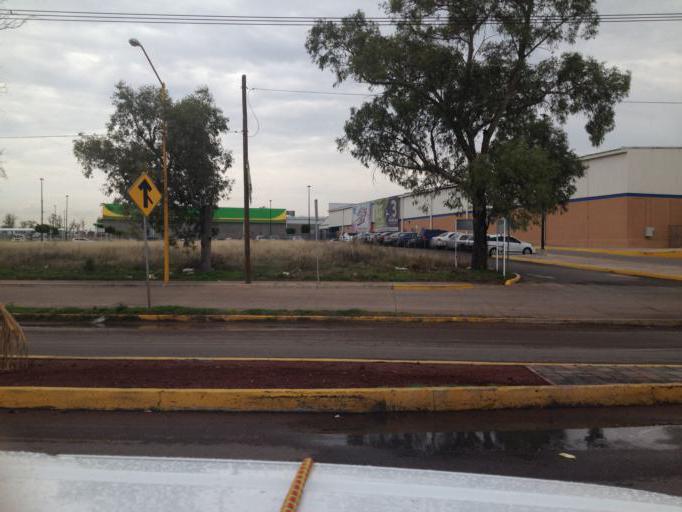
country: MX
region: Aguascalientes
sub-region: Aguascalientes
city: La Loma de los Negritos
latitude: 21.8422
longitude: -102.3240
